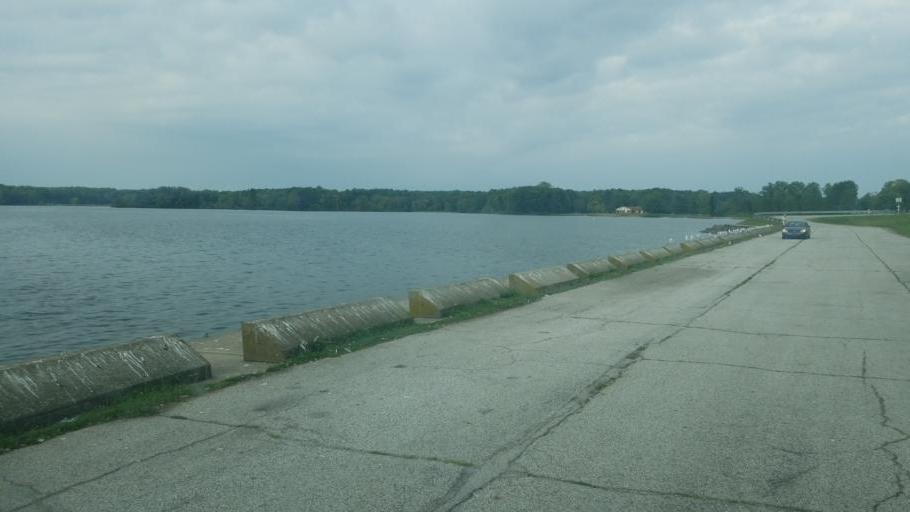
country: US
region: Ohio
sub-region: Ashtabula County
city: Andover
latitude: 41.6070
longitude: -80.5290
